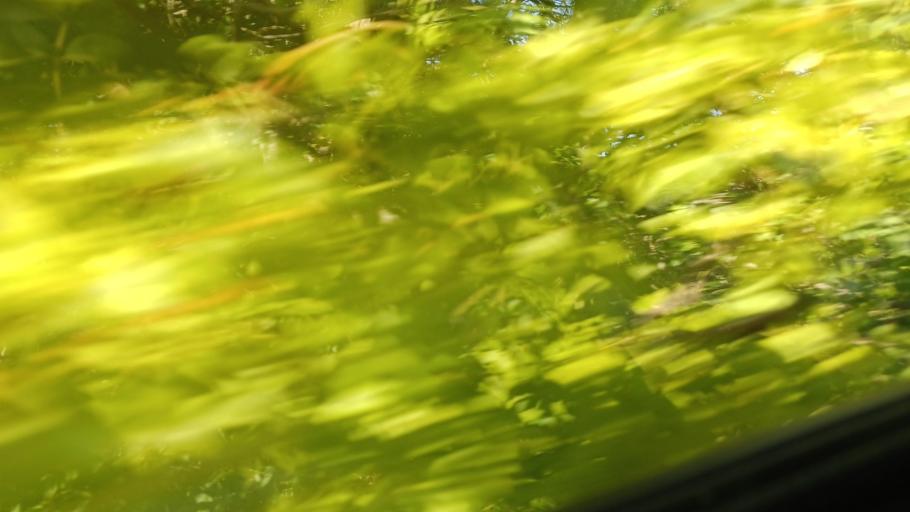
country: CY
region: Pafos
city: Tala
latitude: 34.8885
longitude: 32.4506
